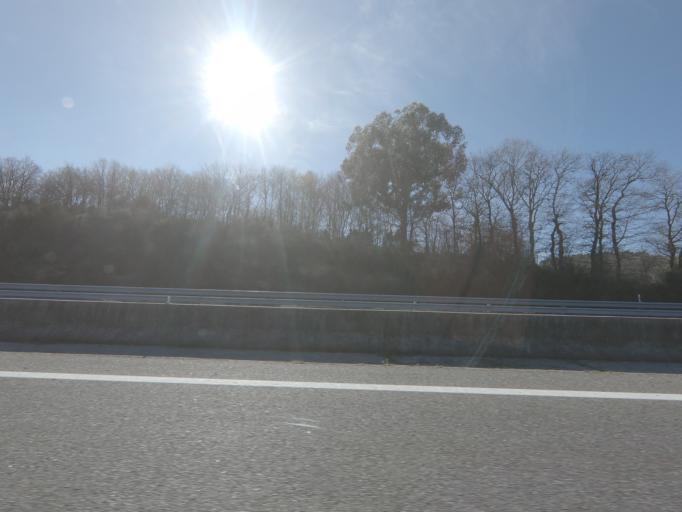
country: ES
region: Galicia
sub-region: Provincia de Pontevedra
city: Dozon
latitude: 42.5584
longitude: -8.0280
